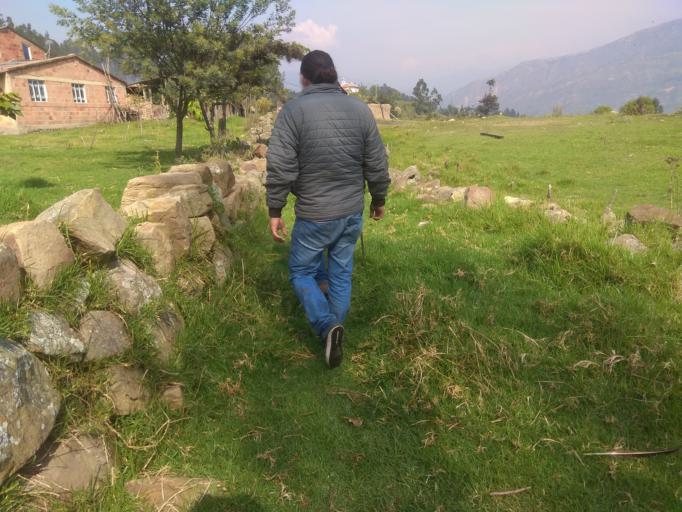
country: CO
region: Boyaca
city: Socha Viejo
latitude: 5.9810
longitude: -72.7070
